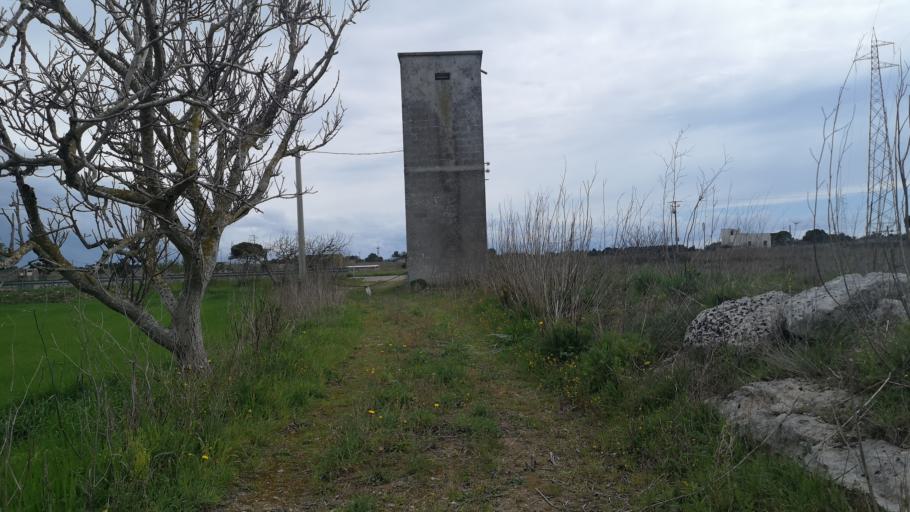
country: IT
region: Apulia
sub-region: Provincia di Lecce
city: Ortelle
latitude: 40.0279
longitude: 18.3808
